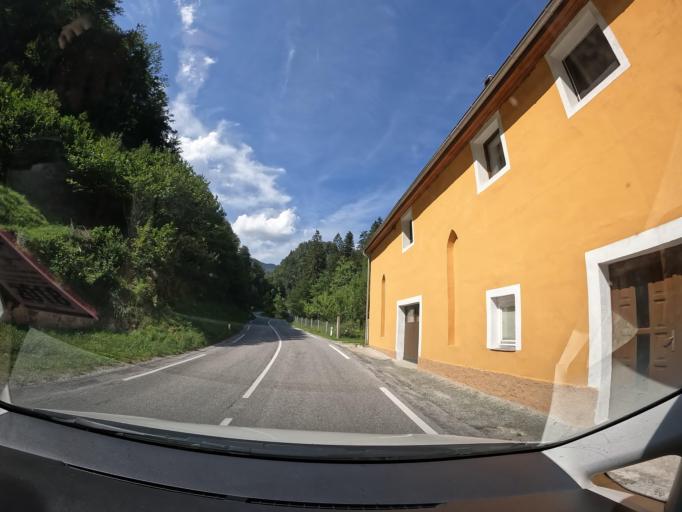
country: SI
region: Kranj
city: Golnik
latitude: 46.3834
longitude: 14.3808
